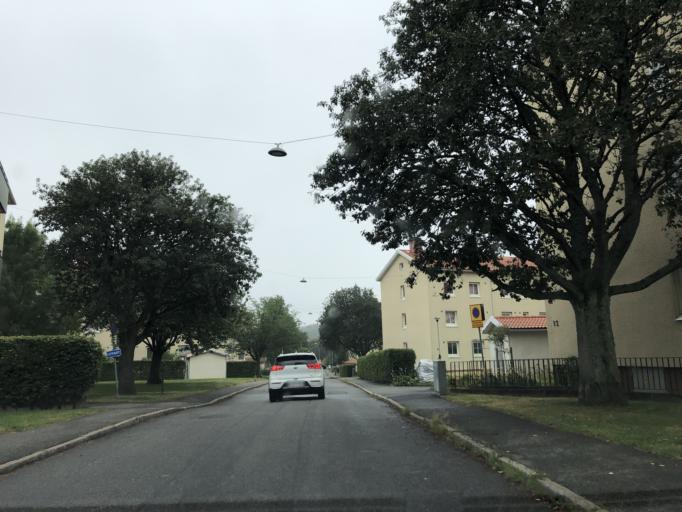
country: SE
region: Vaestra Goetaland
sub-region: Goteborg
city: Goeteborg
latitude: 57.7315
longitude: 11.9337
